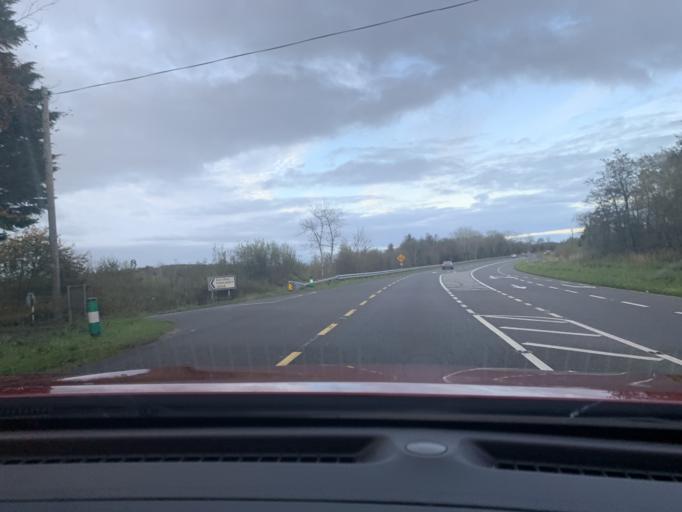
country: IE
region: Connaught
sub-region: Sligo
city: Collooney
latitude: 54.1502
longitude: -8.5451
